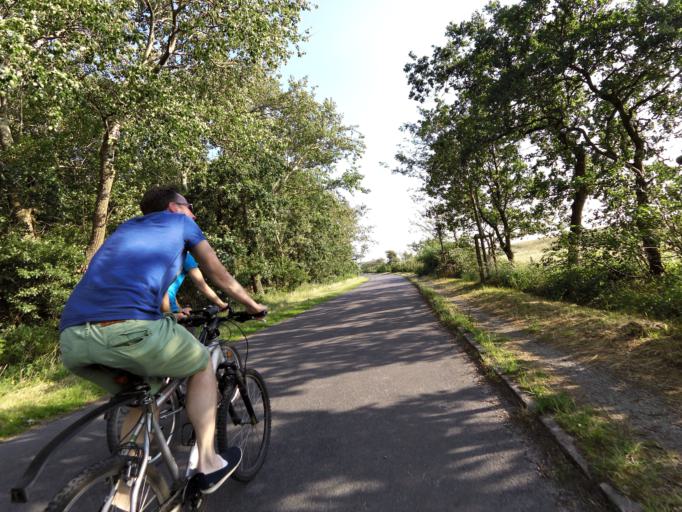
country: DE
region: Lower Saxony
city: Nordholz
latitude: 53.8341
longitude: 8.5806
